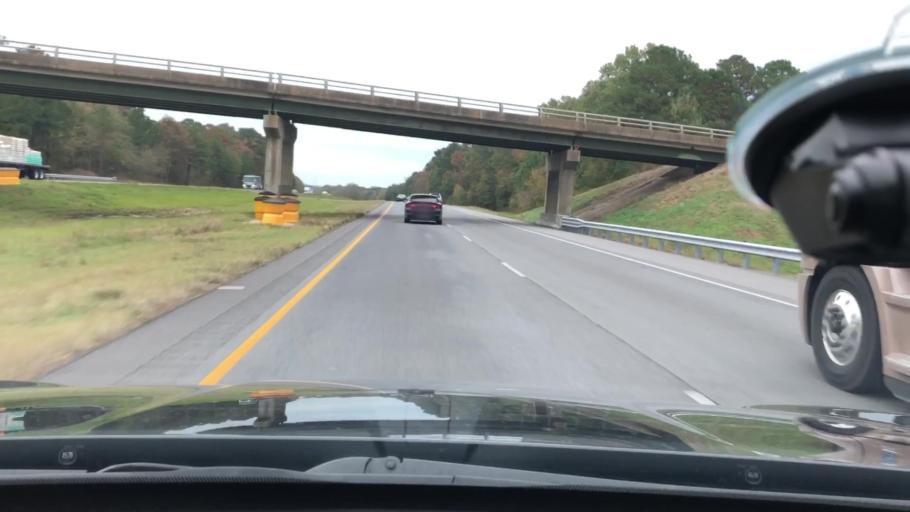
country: US
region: Arkansas
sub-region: Hempstead County
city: Hope
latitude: 33.6298
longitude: -93.7284
